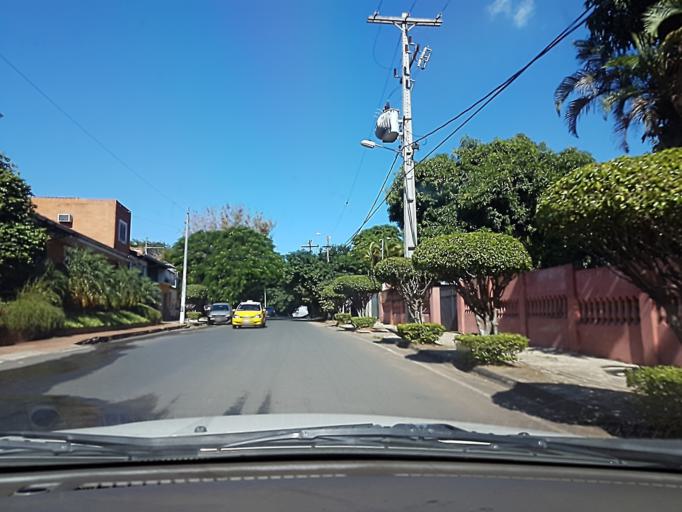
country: PY
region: Central
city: Lambare
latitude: -25.3223
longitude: -57.5875
